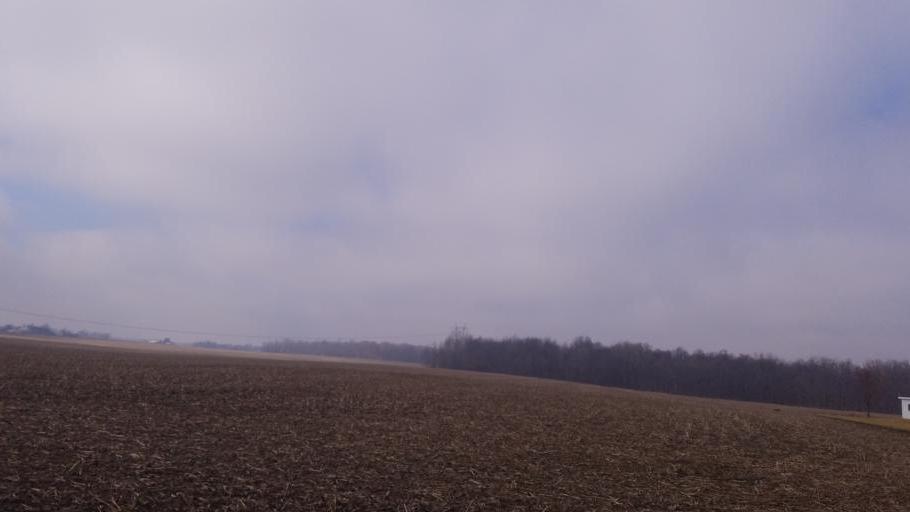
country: US
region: Ohio
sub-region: Crawford County
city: Galion
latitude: 40.7318
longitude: -82.8940
